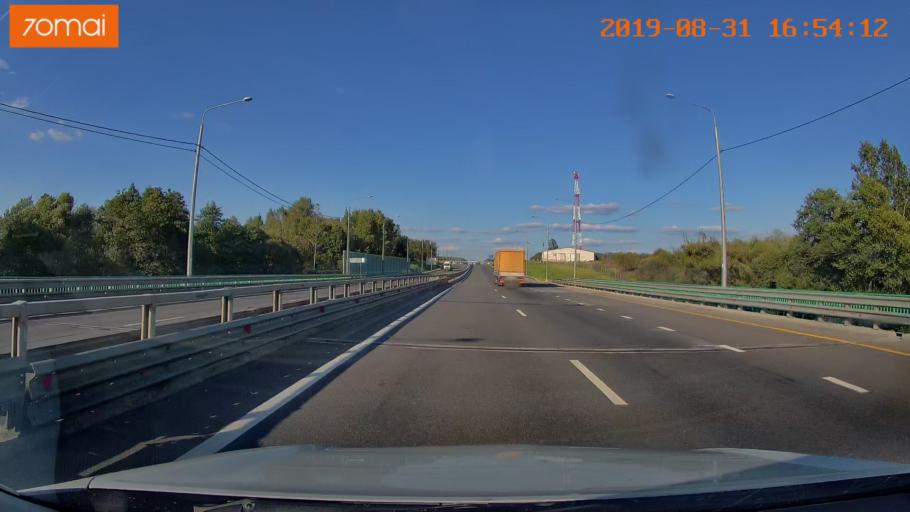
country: RU
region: Kaluga
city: Detchino
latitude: 54.7668
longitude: 36.2278
